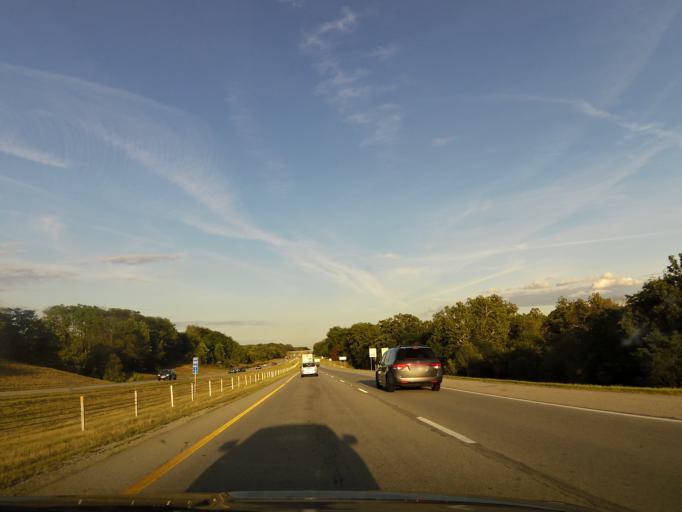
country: US
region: Indiana
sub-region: Boone County
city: Whitestown
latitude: 39.9316
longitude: -86.3352
